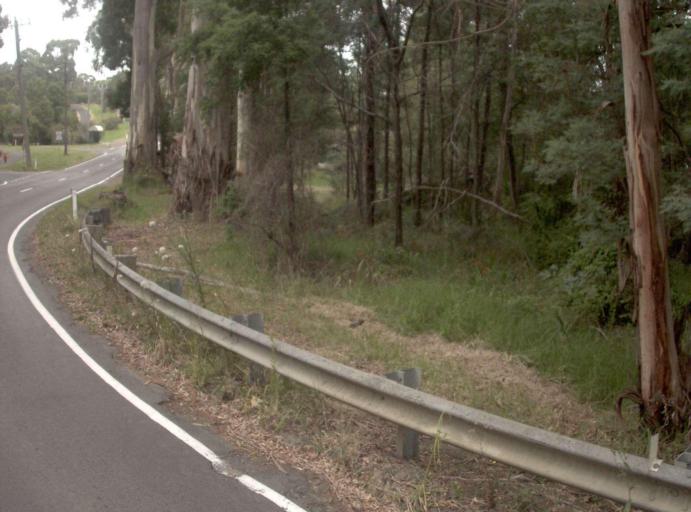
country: AU
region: Victoria
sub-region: Yarra Ranges
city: Badger Creek
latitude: -37.6822
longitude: 145.5356
